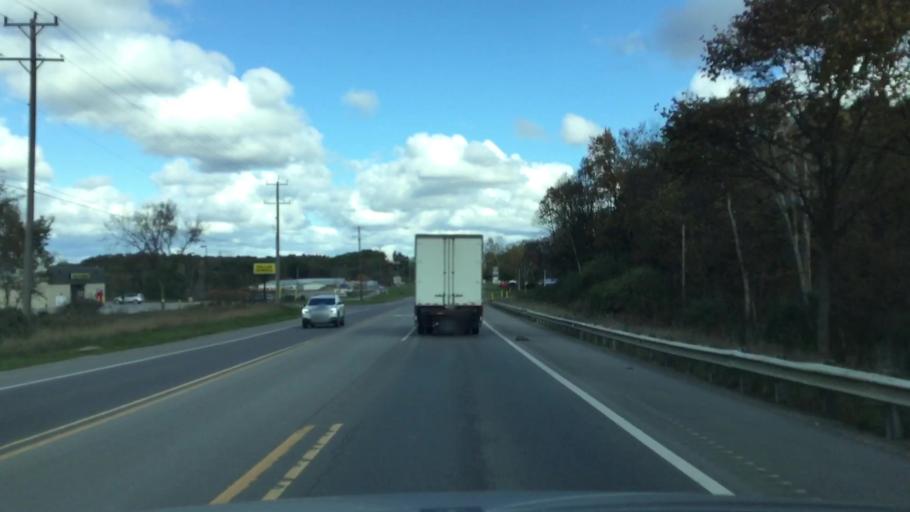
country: US
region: Michigan
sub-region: Lapeer County
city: Lapeer
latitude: 42.9364
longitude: -83.3132
